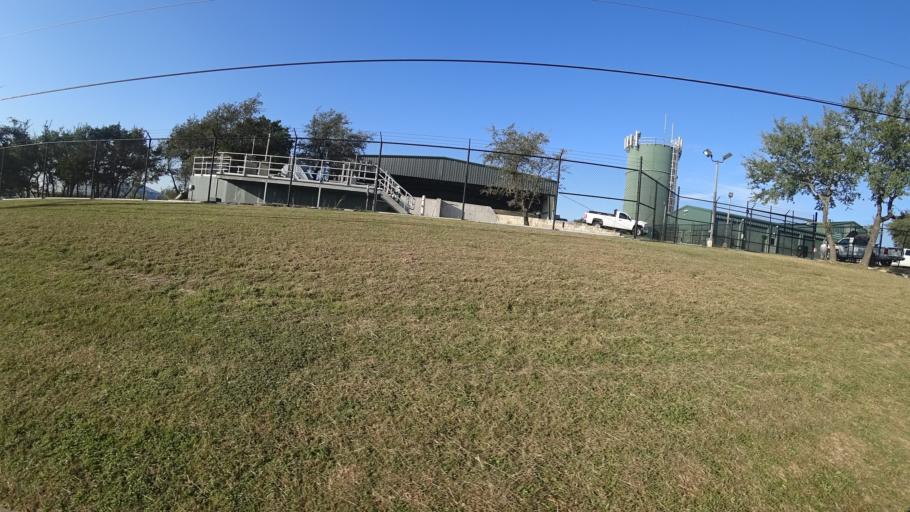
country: US
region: Texas
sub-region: Travis County
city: Hudson Bend
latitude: 30.3686
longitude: -97.8863
